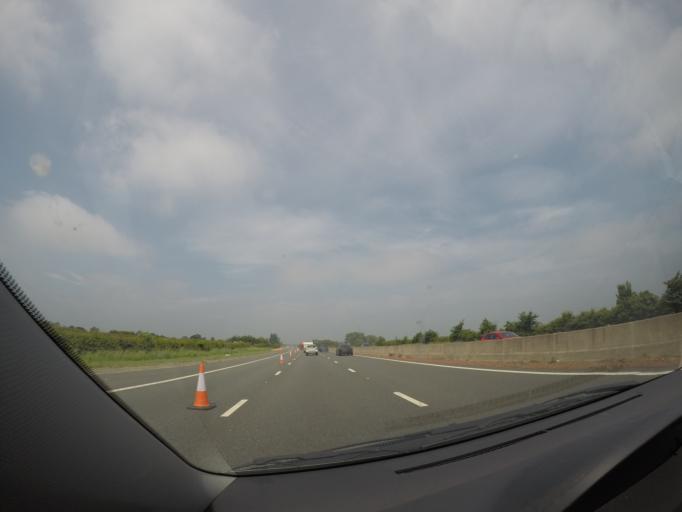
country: GB
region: England
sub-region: North Yorkshire
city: Bedale
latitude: 54.2448
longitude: -1.5024
